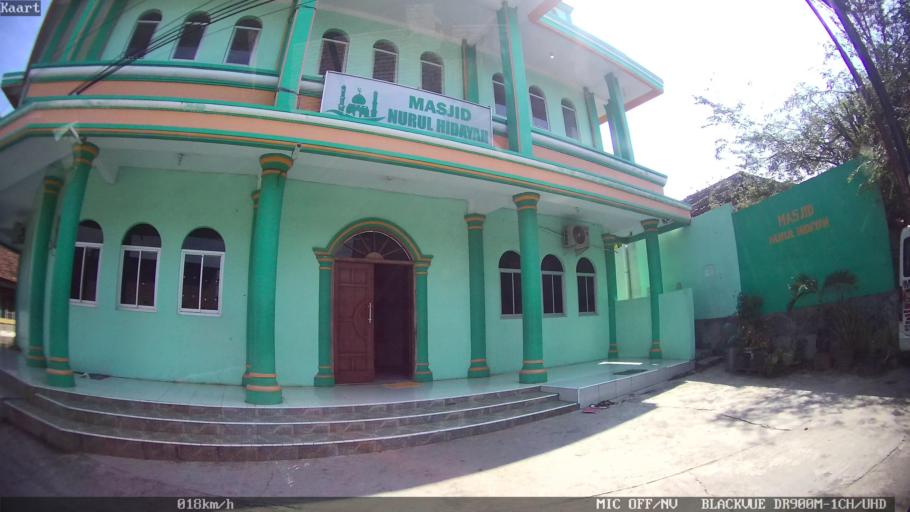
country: ID
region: Lampung
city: Kedaton
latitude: -5.3706
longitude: 105.2497
